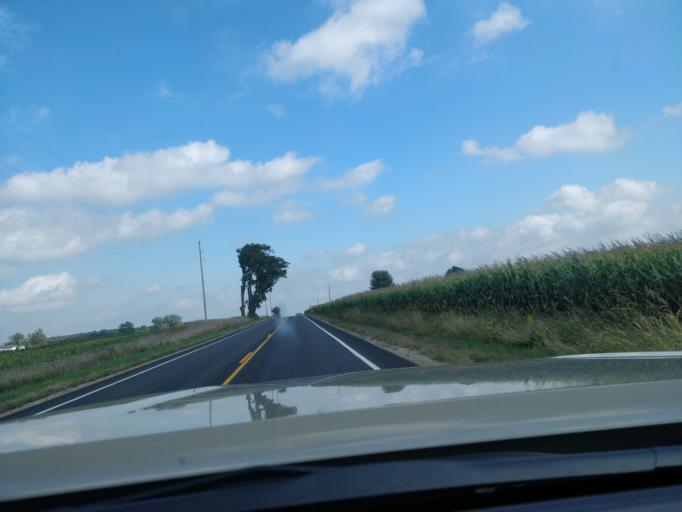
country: US
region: Michigan
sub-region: Ionia County
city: Saranac
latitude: 42.8861
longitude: -85.1234
